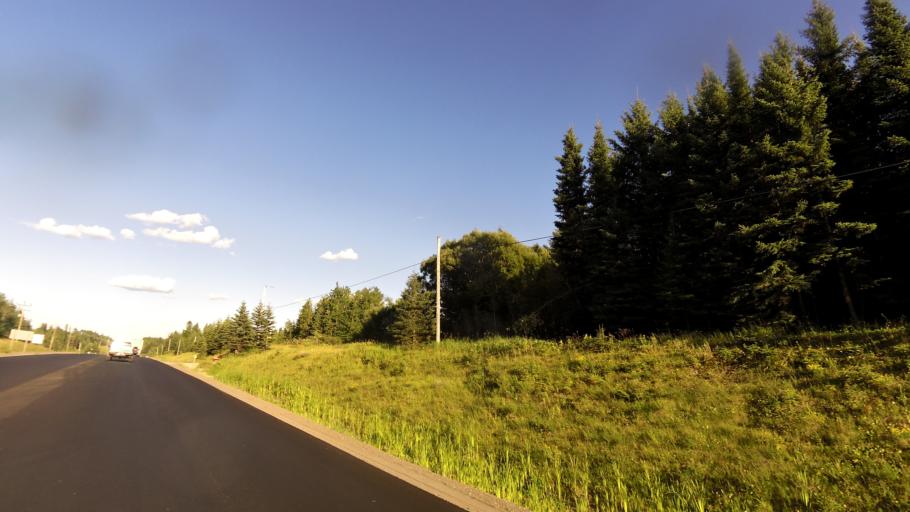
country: CA
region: Ontario
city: Dryden
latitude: 49.8151
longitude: -92.8815
